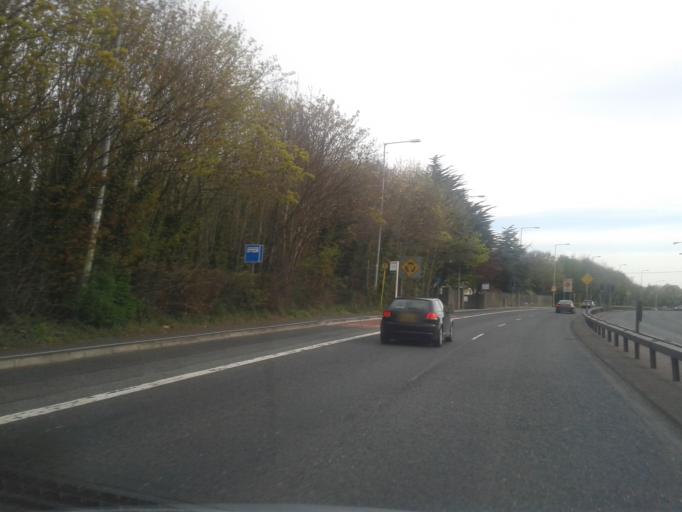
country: IE
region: Leinster
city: Kinsealy-Drinan
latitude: 53.4317
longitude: -6.2301
